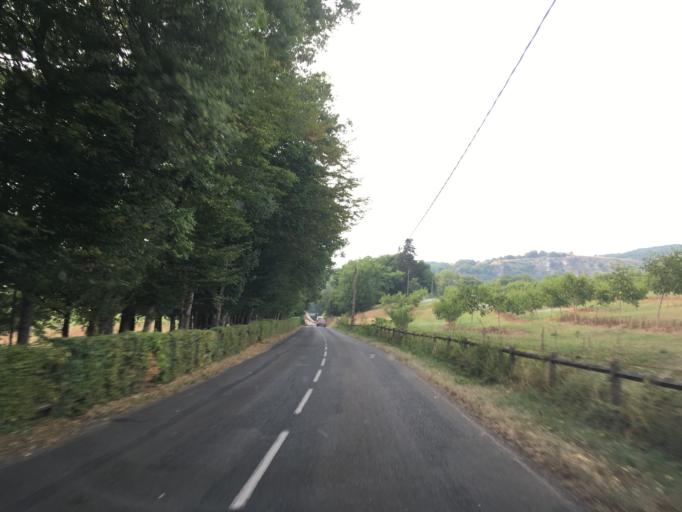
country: FR
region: Midi-Pyrenees
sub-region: Departement du Lot
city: Souillac
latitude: 44.8498
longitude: 1.5300
